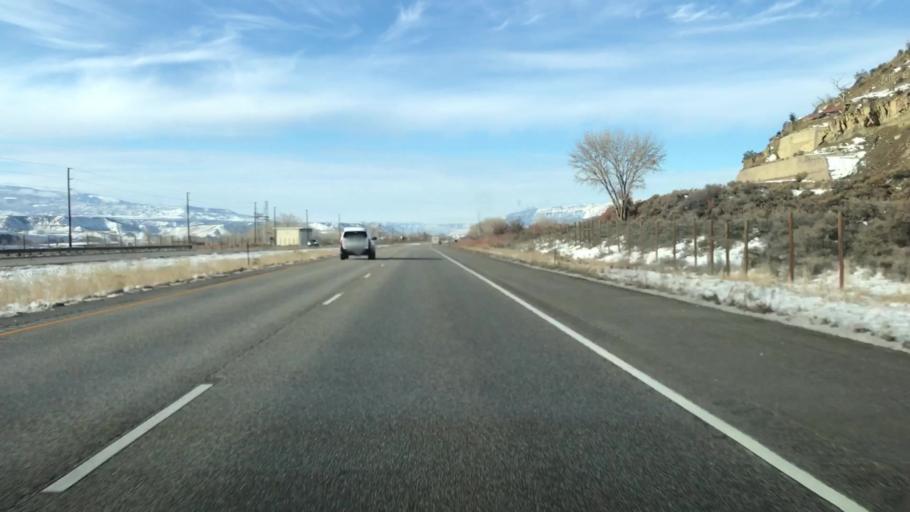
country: US
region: Colorado
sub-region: Garfield County
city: Silt
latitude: 39.5460
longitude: -107.6251
